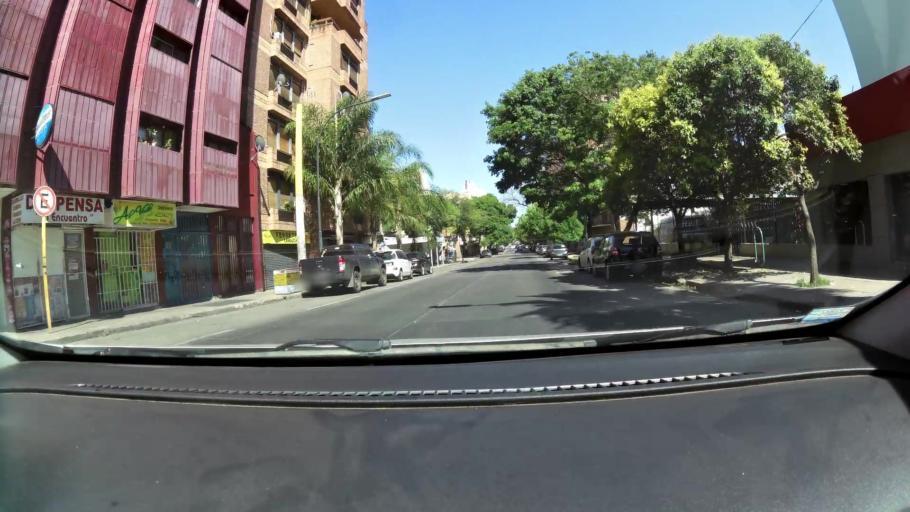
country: AR
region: Cordoba
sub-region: Departamento de Capital
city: Cordoba
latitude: -31.4162
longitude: -64.1962
